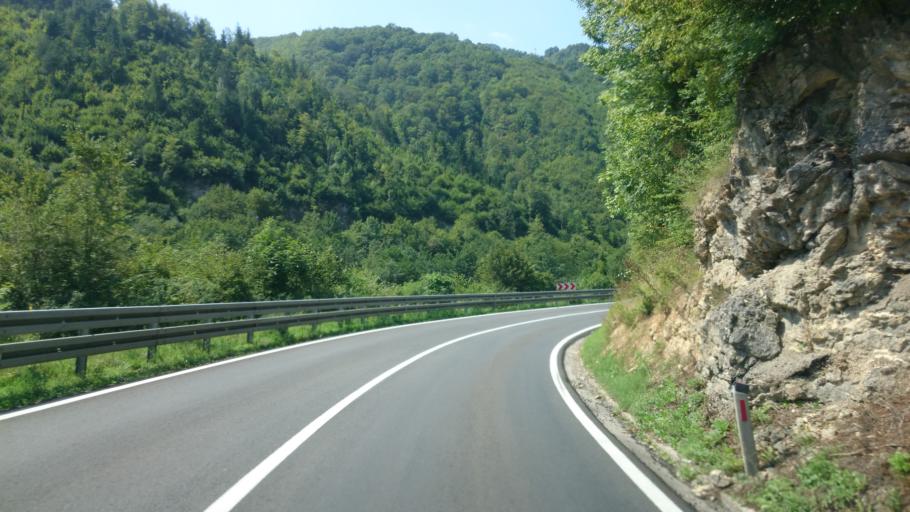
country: BA
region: Federation of Bosnia and Herzegovina
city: Donji Vakuf
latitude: 44.1851
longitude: 17.3453
